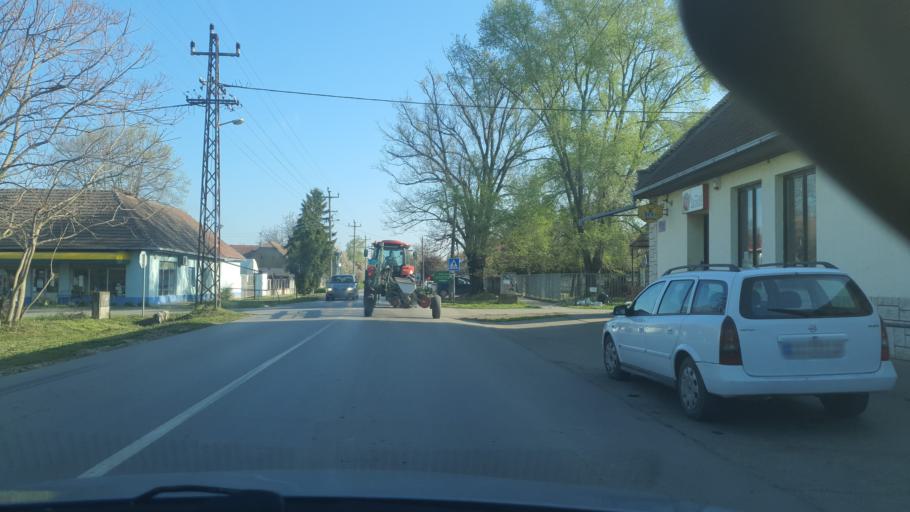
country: RS
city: Kulpin
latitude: 45.4031
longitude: 19.5894
